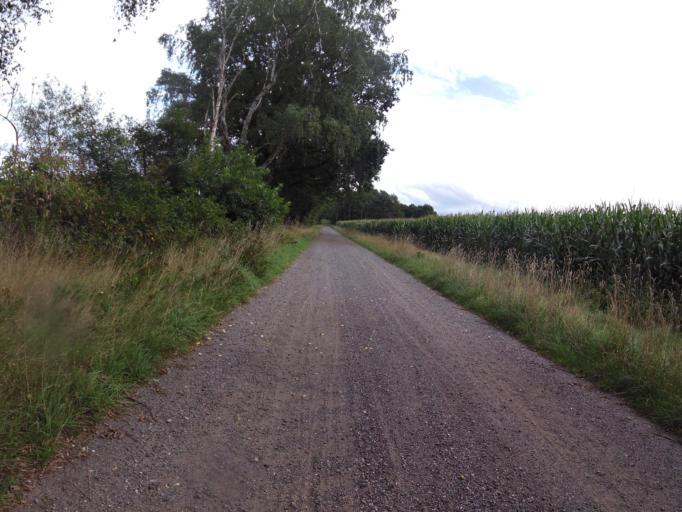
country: DE
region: Lower Saxony
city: Hipstedt
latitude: 53.5015
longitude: 8.9189
